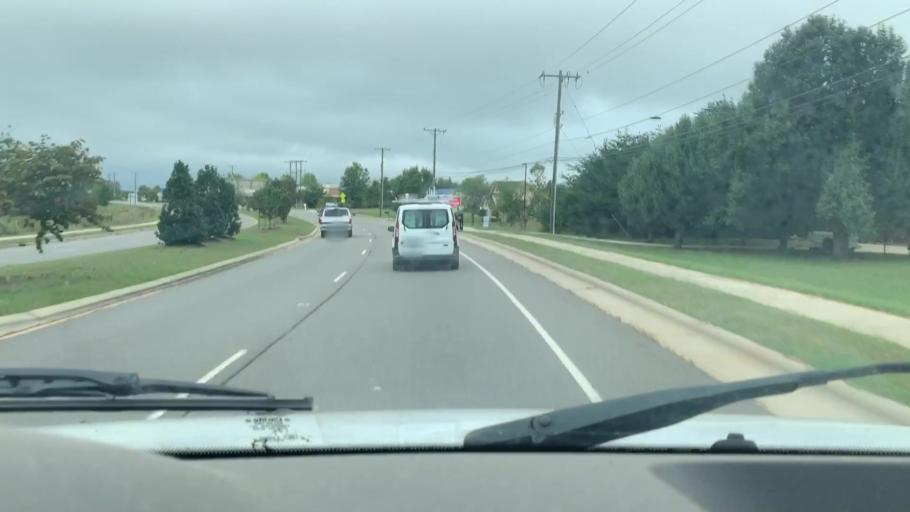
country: US
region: North Carolina
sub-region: Iredell County
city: Mooresville
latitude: 35.5842
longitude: -80.8672
